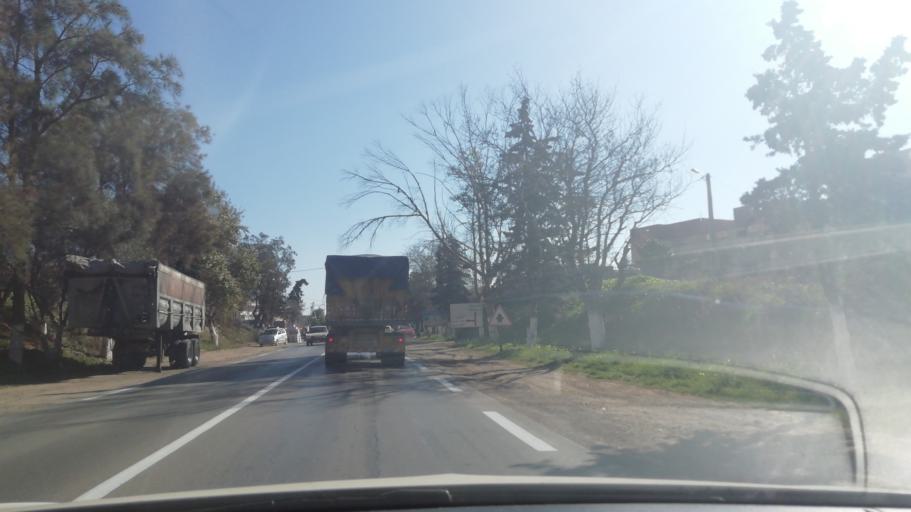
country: DZ
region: Tlemcen
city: Nedroma
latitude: 35.0871
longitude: -1.8043
